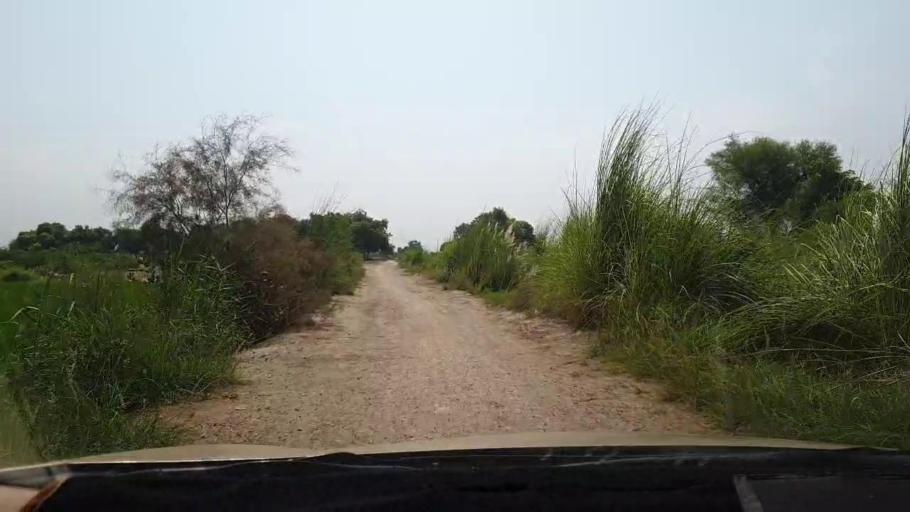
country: PK
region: Sindh
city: Larkana
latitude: 27.6366
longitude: 68.2425
